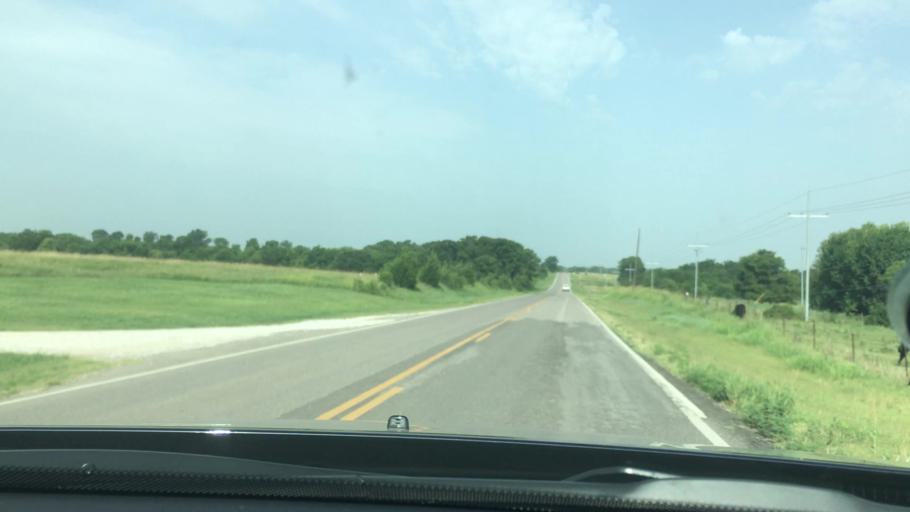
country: US
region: Oklahoma
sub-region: Garvin County
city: Stratford
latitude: 34.7967
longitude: -96.9186
